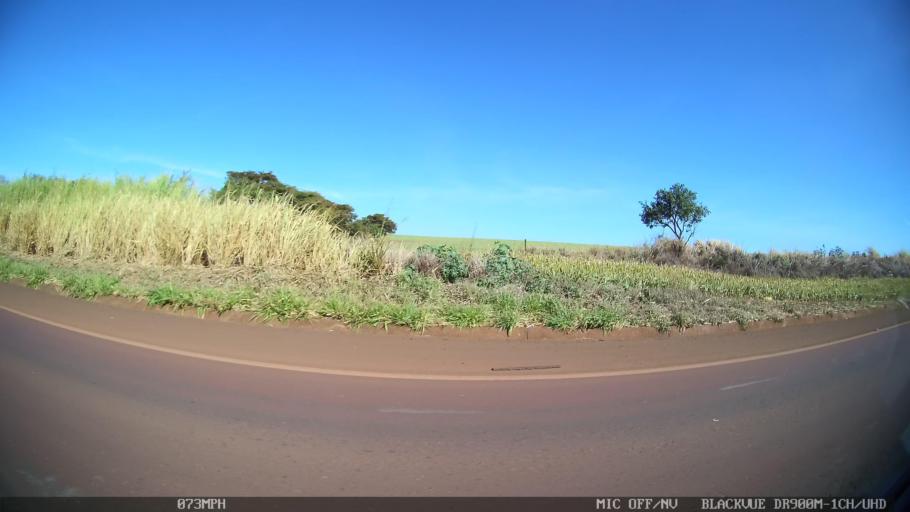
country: BR
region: Sao Paulo
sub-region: Ipua
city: Ipua
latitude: -20.4909
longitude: -48.0533
